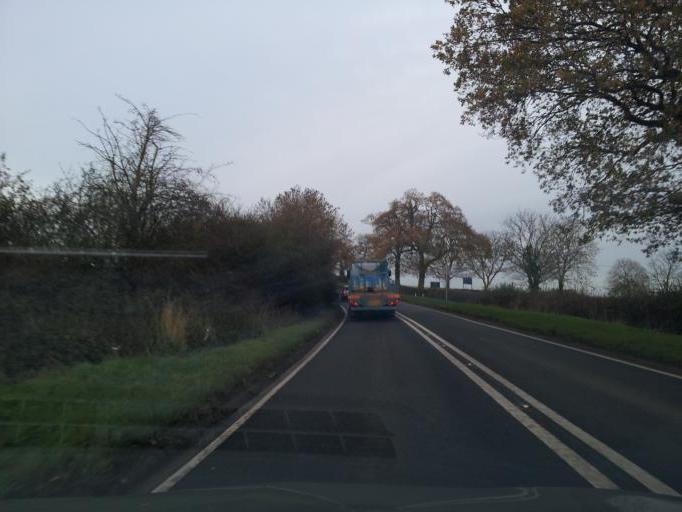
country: GB
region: England
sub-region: Buckinghamshire
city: Stewkley
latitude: 51.8820
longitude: -0.7319
